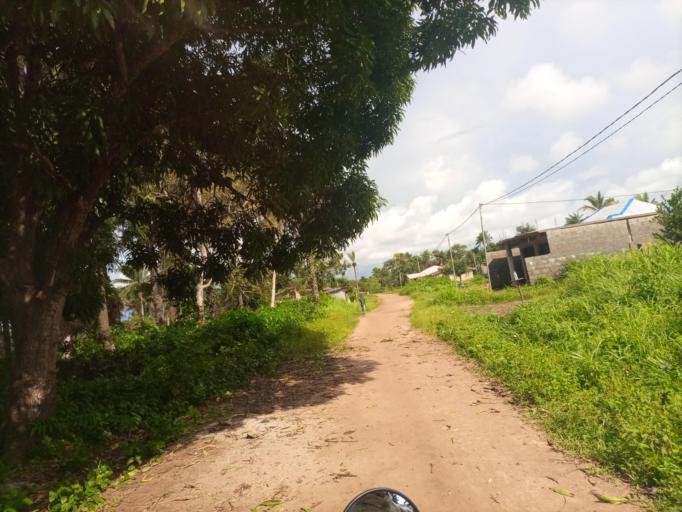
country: SL
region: Northern Province
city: Masoyila
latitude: 8.6241
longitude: -13.1745
